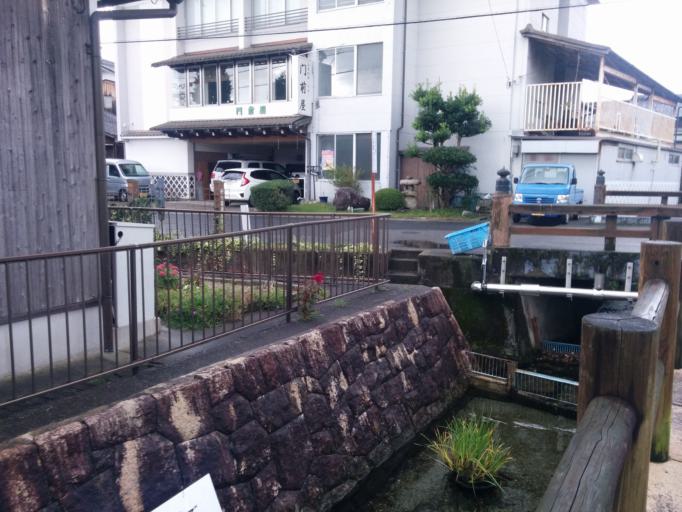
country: JP
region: Shiga Prefecture
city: Omihachiman
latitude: 35.1440
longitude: 136.1296
